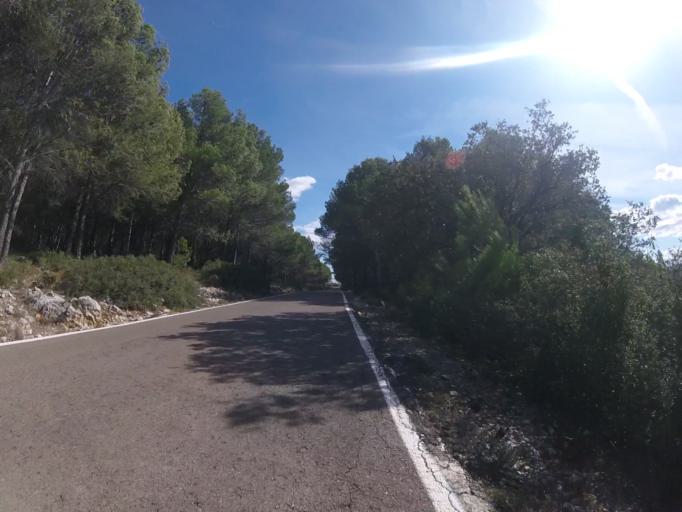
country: ES
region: Valencia
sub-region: Provincia de Castello
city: Albocasser
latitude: 40.4045
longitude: 0.0794
